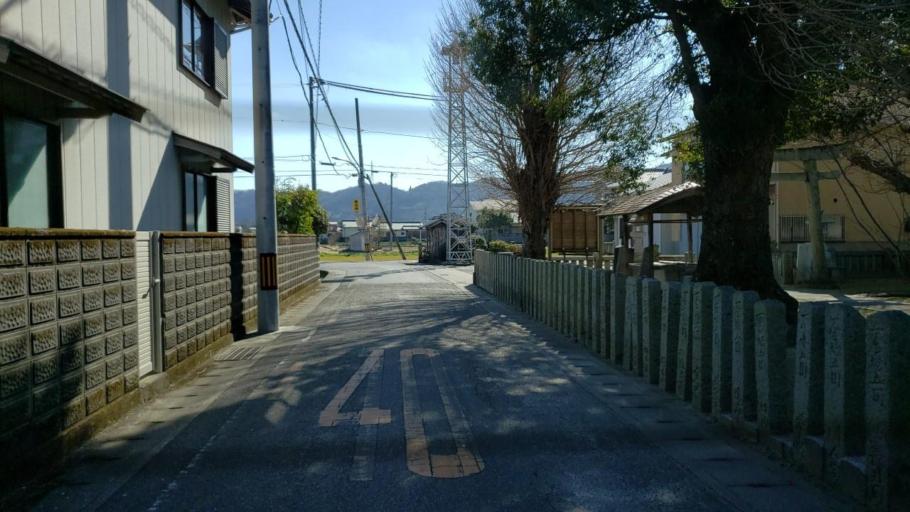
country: JP
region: Tokushima
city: Ishii
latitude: 34.0719
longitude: 134.4324
